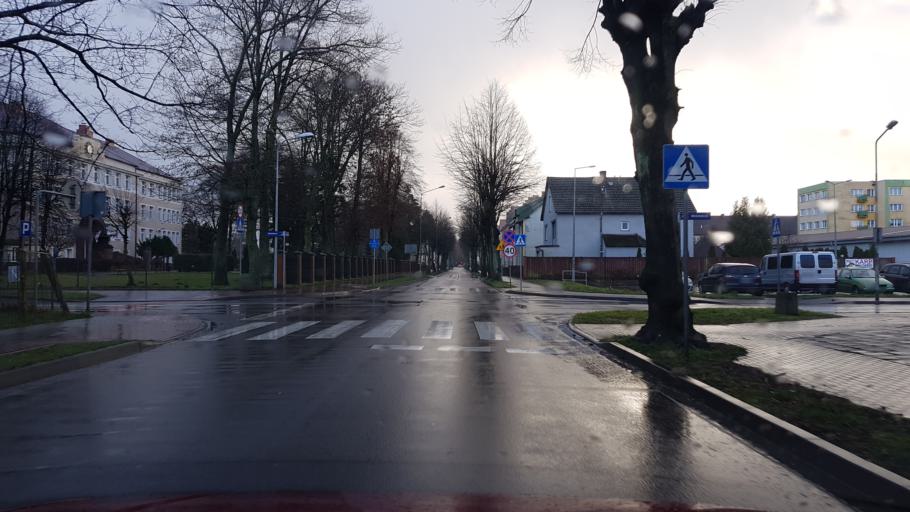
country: PL
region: West Pomeranian Voivodeship
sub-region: Powiat bialogardzki
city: Bialogard
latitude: 54.0114
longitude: 15.9906
